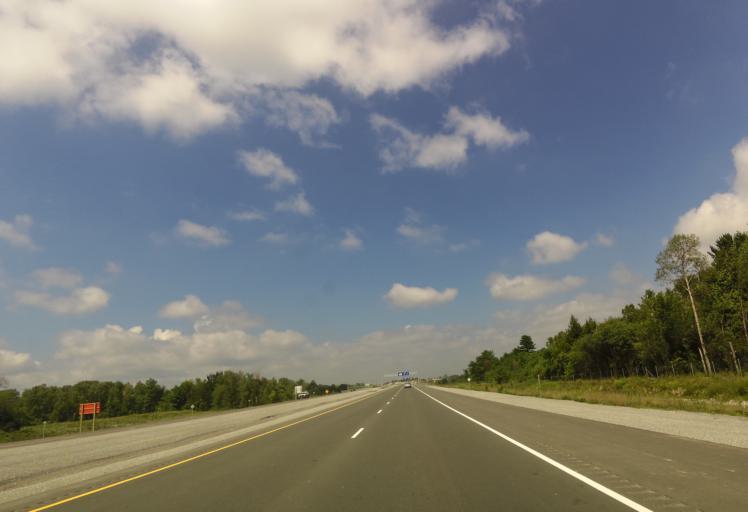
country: CA
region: Ontario
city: Ajax
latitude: 43.9313
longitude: -79.0020
